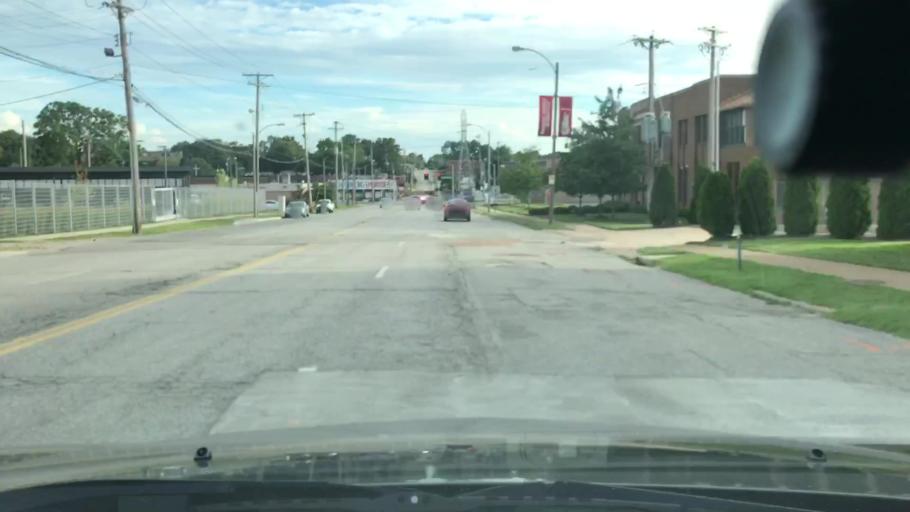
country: US
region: Missouri
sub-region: Saint Louis County
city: Richmond Heights
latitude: 38.6256
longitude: -90.2754
